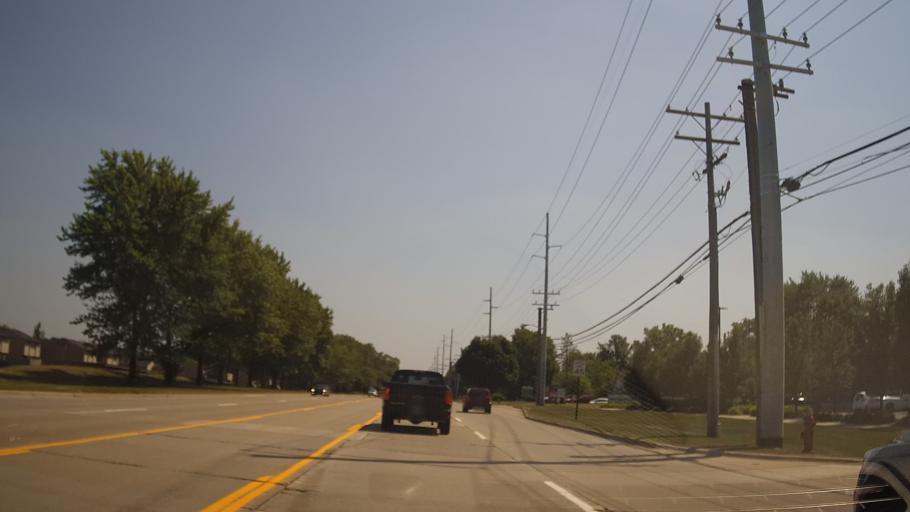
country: US
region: Michigan
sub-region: Oakland County
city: Troy
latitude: 42.6152
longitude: -83.1303
